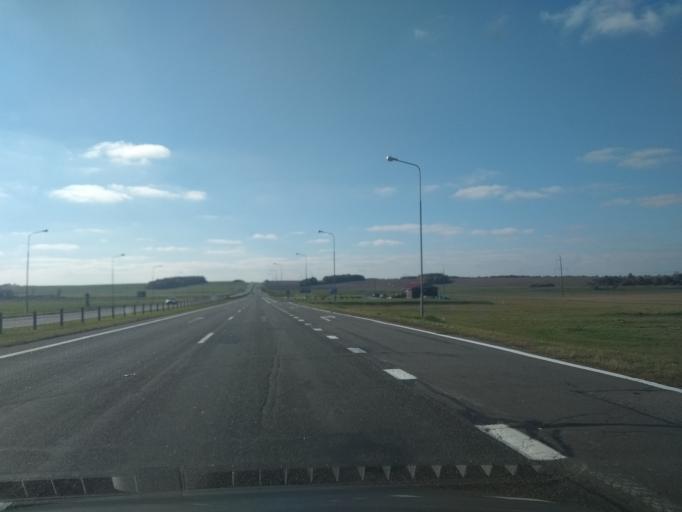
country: BY
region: Minsk
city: Haradzyeya
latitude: 53.3428
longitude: 26.4439
